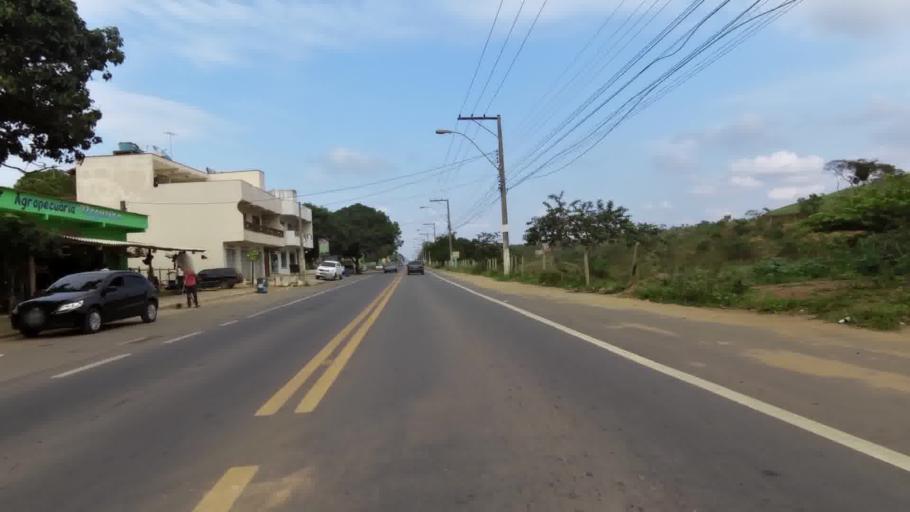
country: BR
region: Espirito Santo
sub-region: Piuma
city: Piuma
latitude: -20.8332
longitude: -40.7120
